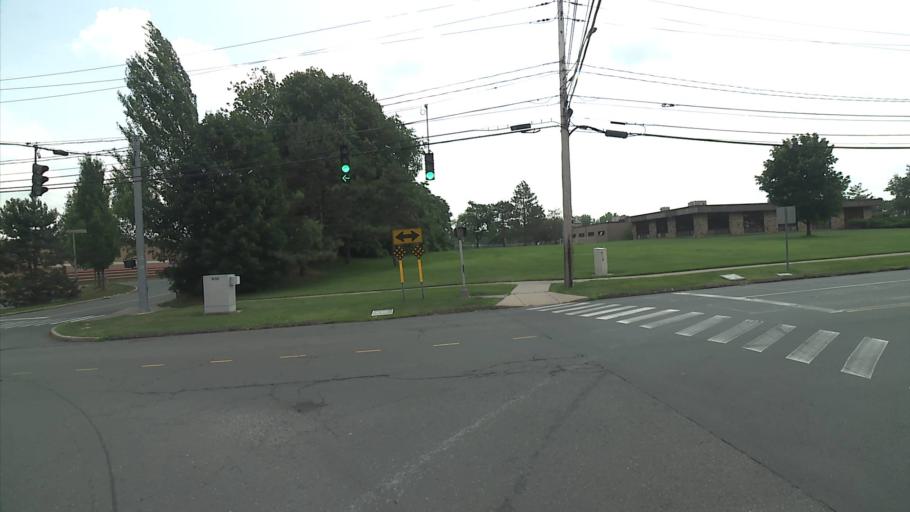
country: US
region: Connecticut
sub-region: Hartford County
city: Newington
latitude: 41.6619
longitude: -72.7266
